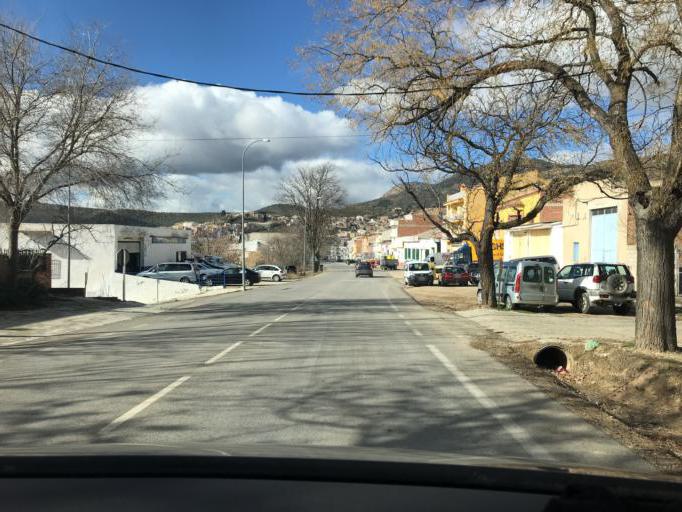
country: ES
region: Andalusia
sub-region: Provincia de Jaen
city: Huelma
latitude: 37.6490
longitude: -3.4477
